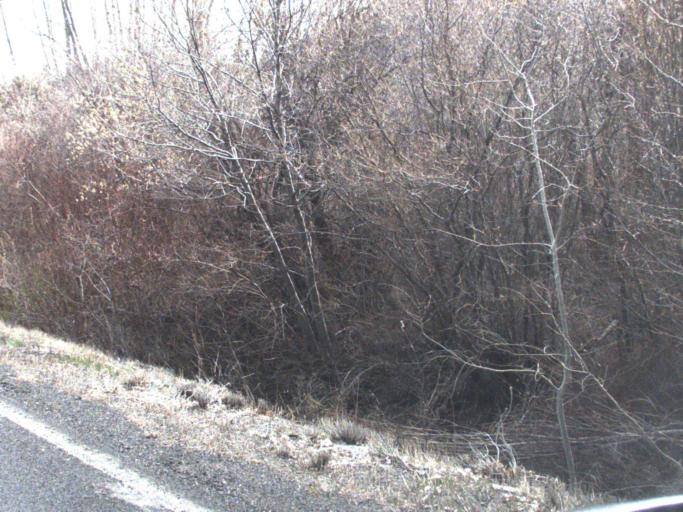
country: US
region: Washington
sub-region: Yakima County
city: Tieton
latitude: 46.7984
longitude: -120.8960
